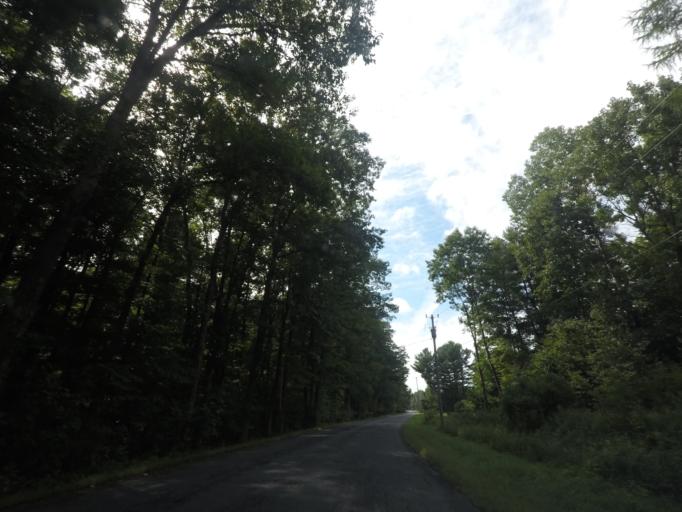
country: US
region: New York
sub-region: Rensselaer County
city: Nassau
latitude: 42.5643
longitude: -73.6186
